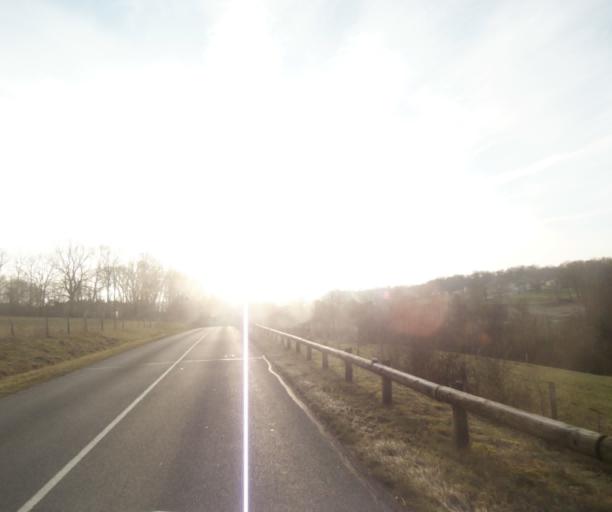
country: FR
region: Champagne-Ardenne
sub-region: Departement de la Marne
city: Sermaize-les-Bains
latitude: 48.7252
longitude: 4.9381
